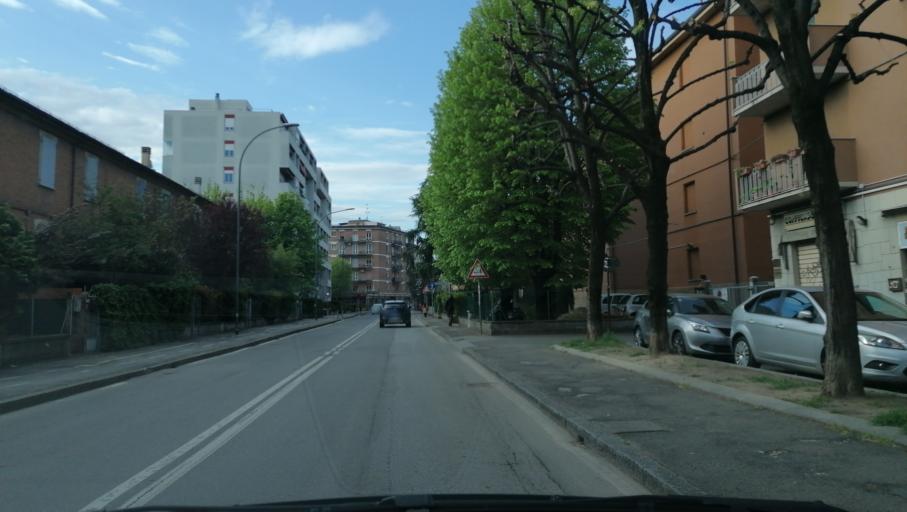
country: IT
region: Emilia-Romagna
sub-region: Provincia di Bologna
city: Bologna
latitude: 44.5151
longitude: 11.3423
